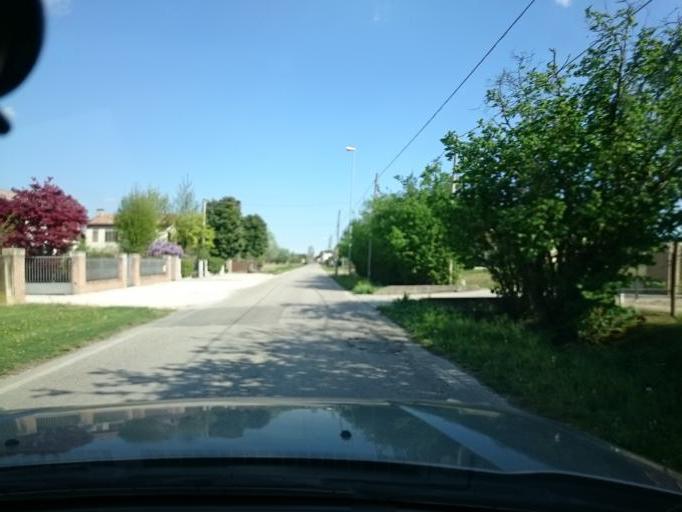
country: IT
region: Veneto
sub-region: Provincia di Venezia
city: Sant'Angelo
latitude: 45.5173
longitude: 12.0016
